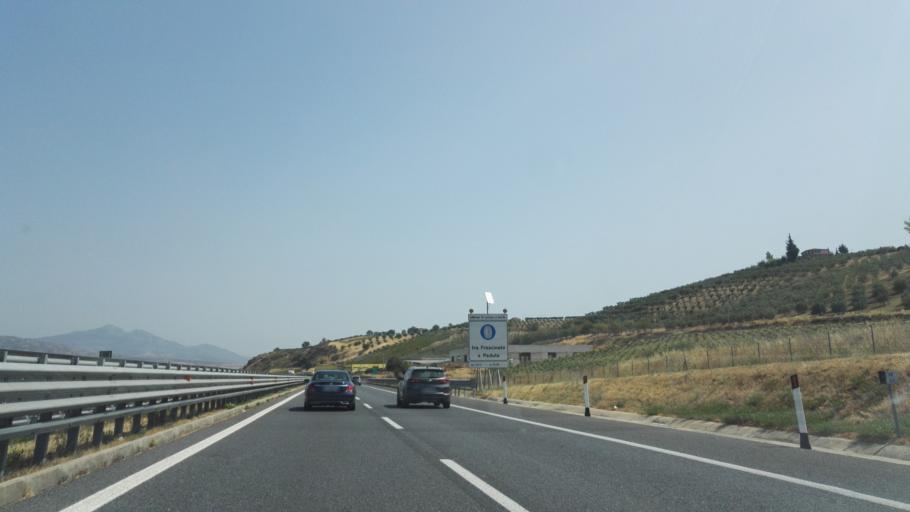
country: IT
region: Calabria
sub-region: Provincia di Cosenza
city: San Lorenzo del Vallo
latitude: 39.6907
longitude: 16.2316
